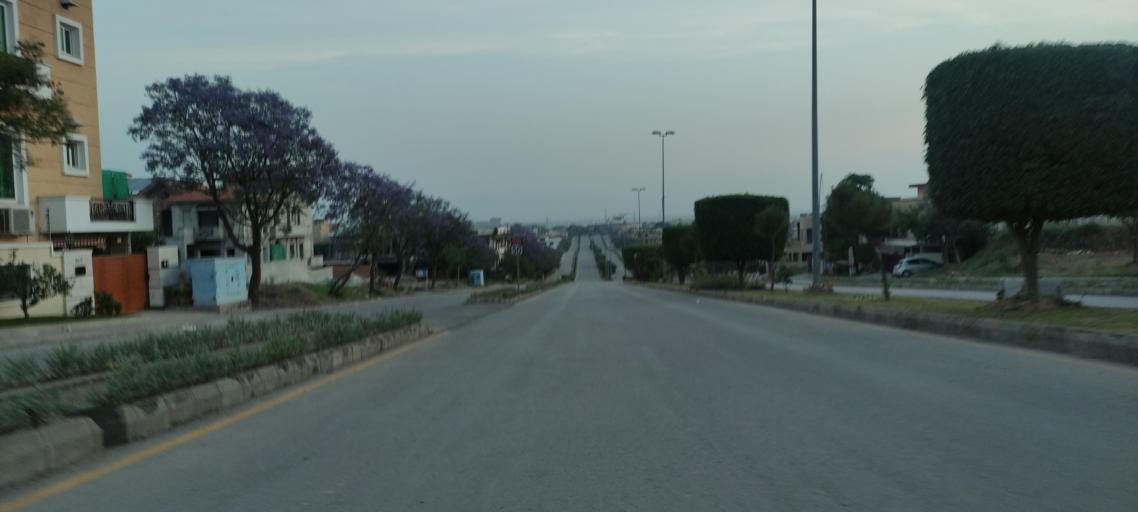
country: PK
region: Punjab
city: Rawalpindi
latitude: 33.5214
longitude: 73.1651
